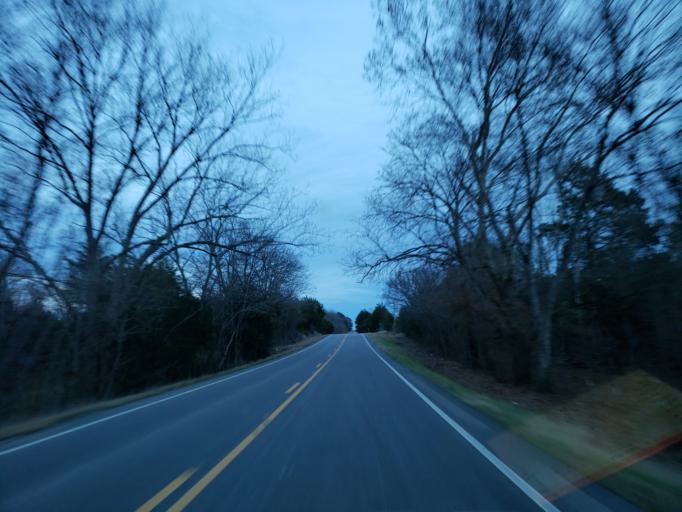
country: US
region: Alabama
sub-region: Sumter County
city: Livingston
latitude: 32.8110
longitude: -88.2620
